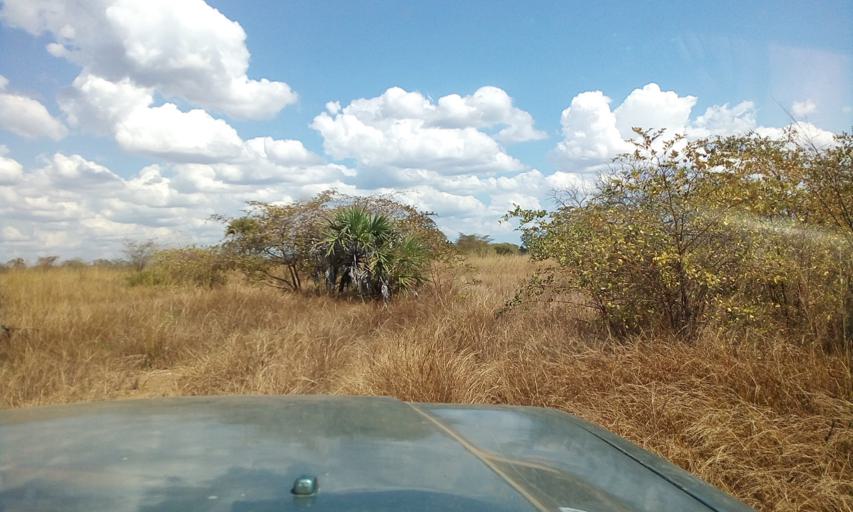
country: MG
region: Melaky
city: Mahabe
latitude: -16.4367
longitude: 45.3808
